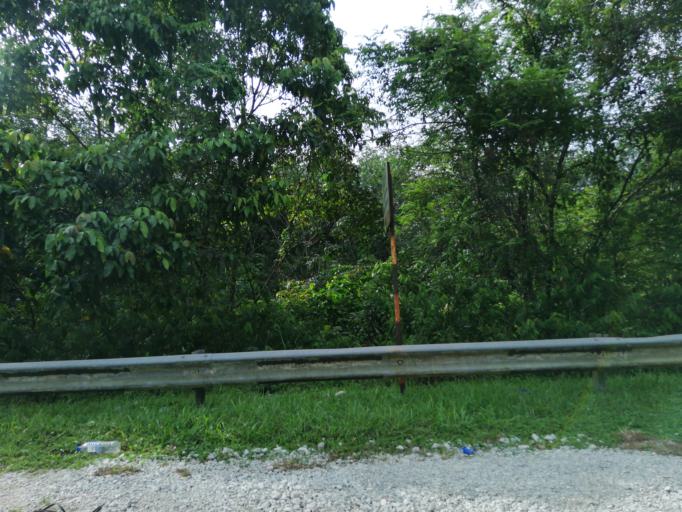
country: MY
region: Penang
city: Tasek Glugor
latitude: 5.4994
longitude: 100.6123
